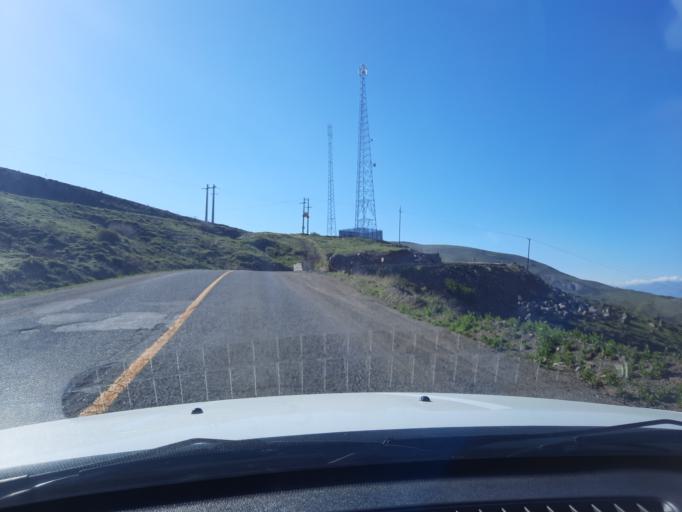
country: IR
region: Qazvin
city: Qazvin
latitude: 36.4061
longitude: 50.2226
